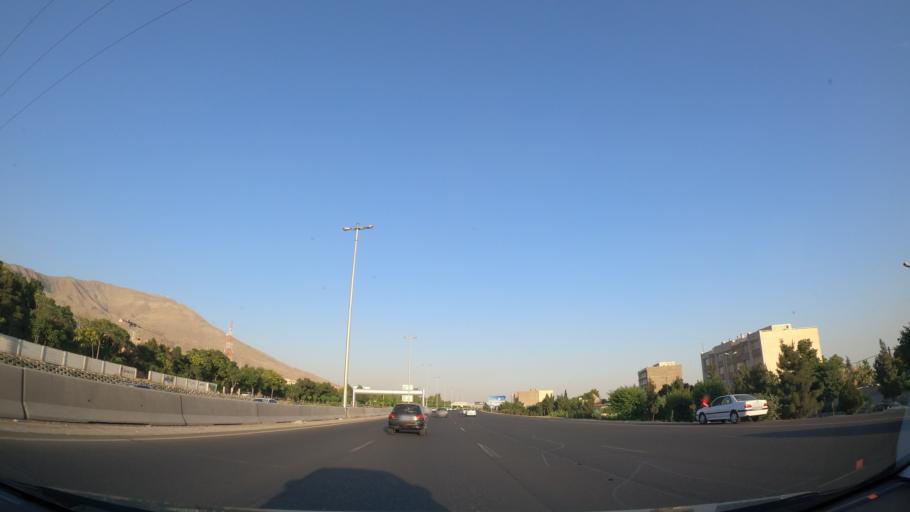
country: IR
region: Alborz
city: Karaj
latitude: 35.7859
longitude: 51.0258
